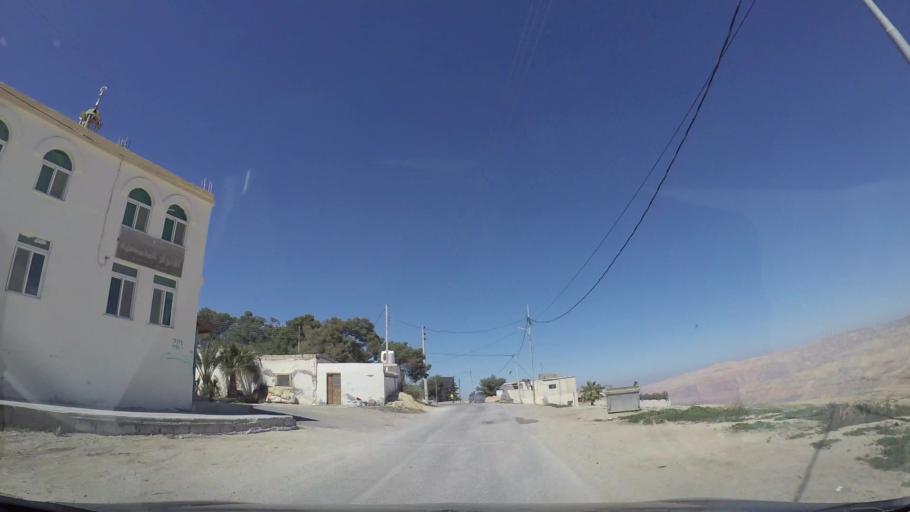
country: JO
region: Tafielah
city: At Tafilah
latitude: 30.8407
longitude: 35.5688
